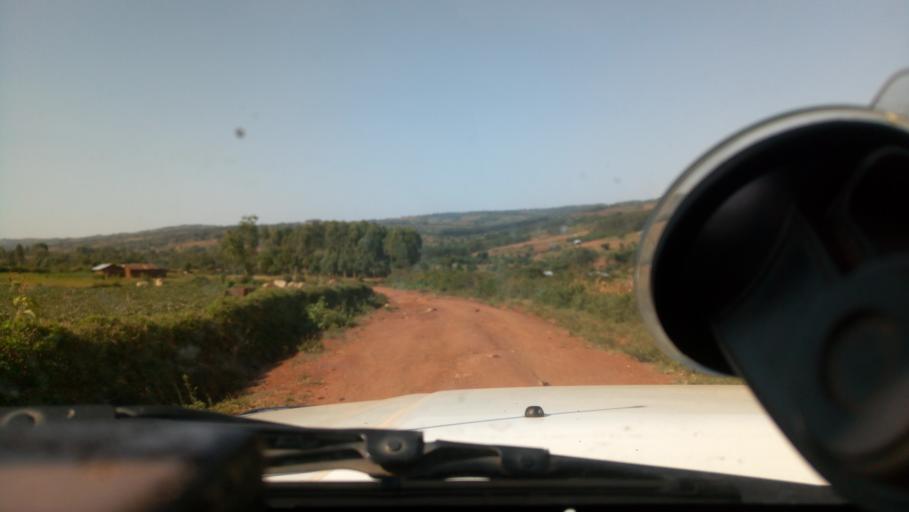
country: TZ
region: Mara
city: Sirari
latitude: -1.2313
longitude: 34.5312
